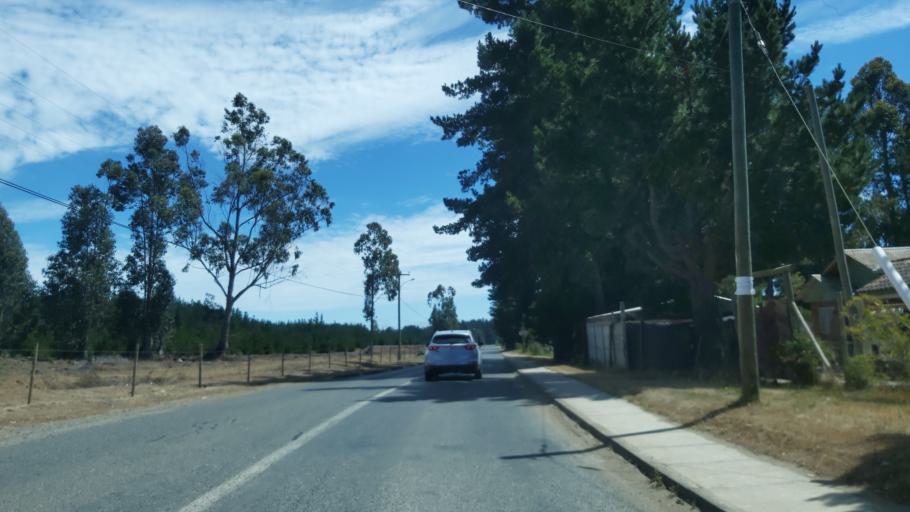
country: CL
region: Maule
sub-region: Provincia de Talca
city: Constitucion
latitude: -35.5081
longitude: -72.5213
